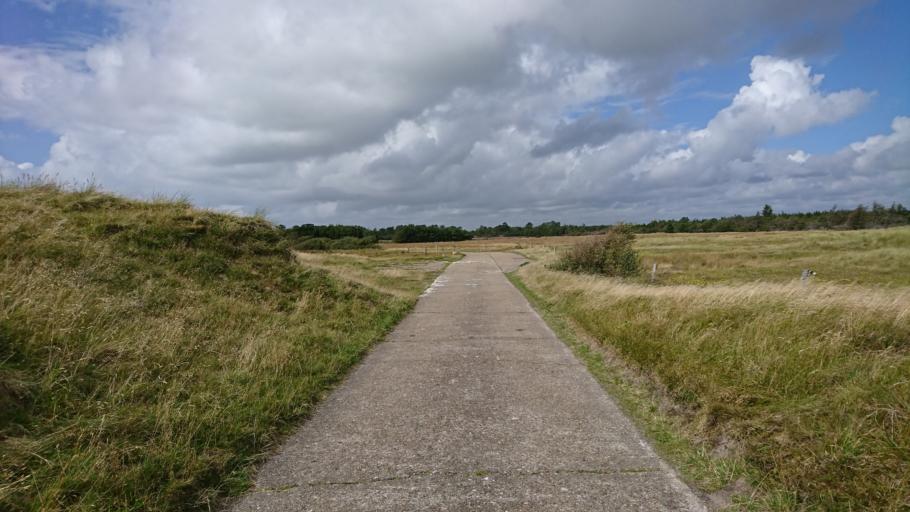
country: DK
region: South Denmark
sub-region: Fano Kommune
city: Nordby
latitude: 55.3838
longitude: 8.4194
